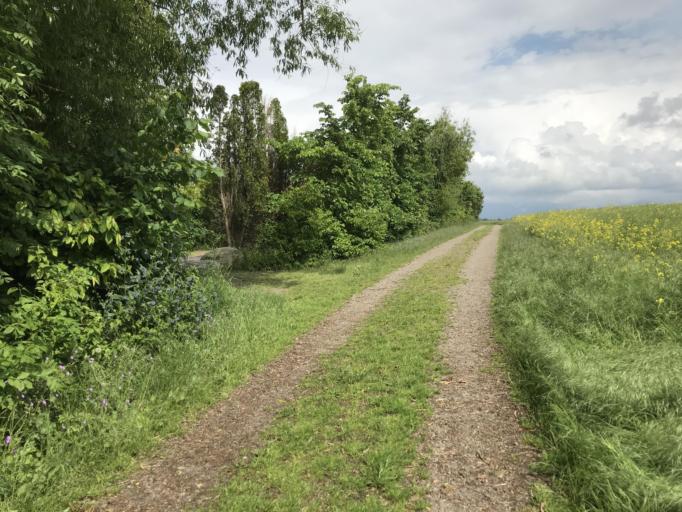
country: SE
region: Skane
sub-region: Landskrona
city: Landskrona
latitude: 55.8998
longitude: 12.8342
